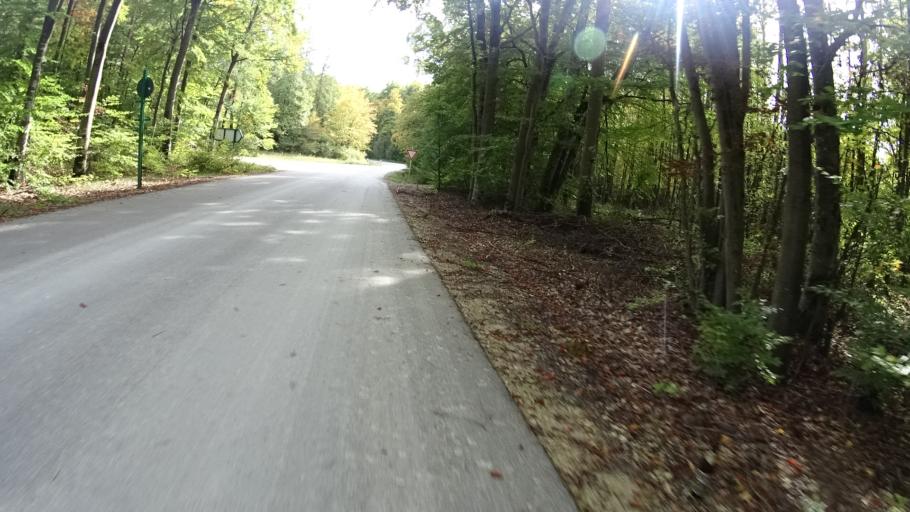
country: DE
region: Bavaria
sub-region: Upper Bavaria
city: Walting
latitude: 48.9055
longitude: 11.3245
